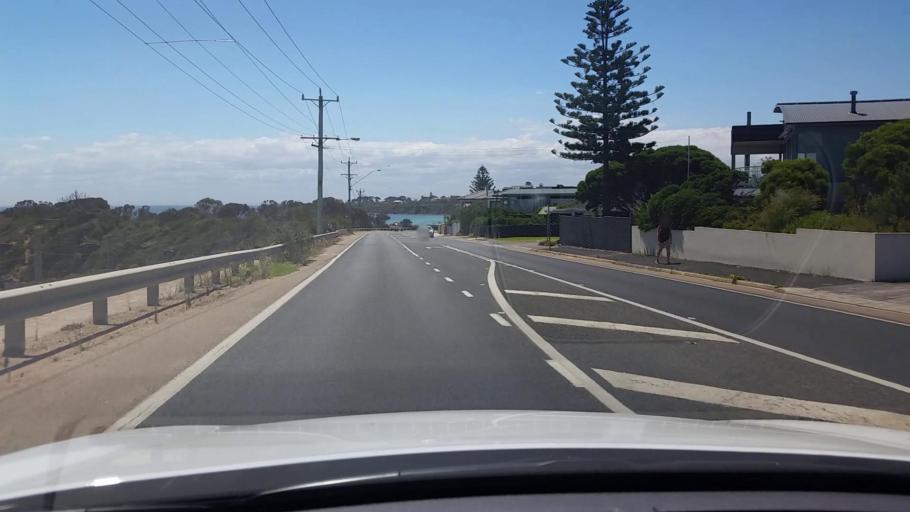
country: AU
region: Victoria
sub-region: Mornington Peninsula
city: Mornington
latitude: -38.2289
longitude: 145.0265
